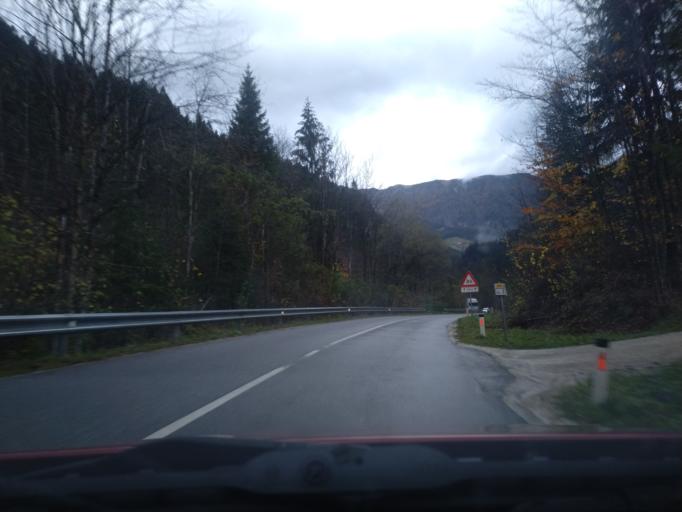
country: SI
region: Solcava
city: Solcava
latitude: 46.4067
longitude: 14.7015
